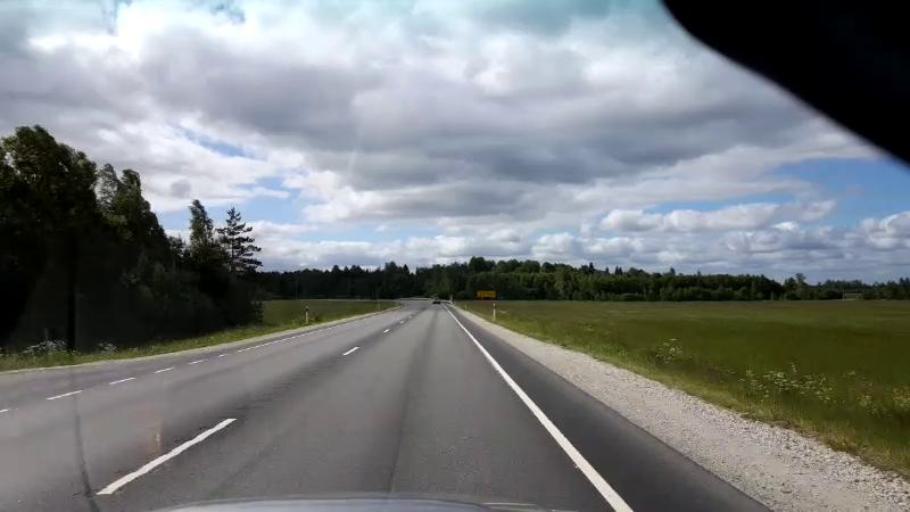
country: EE
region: Paernumaa
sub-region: Halinga vald
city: Parnu-Jaagupi
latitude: 58.6749
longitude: 24.4435
